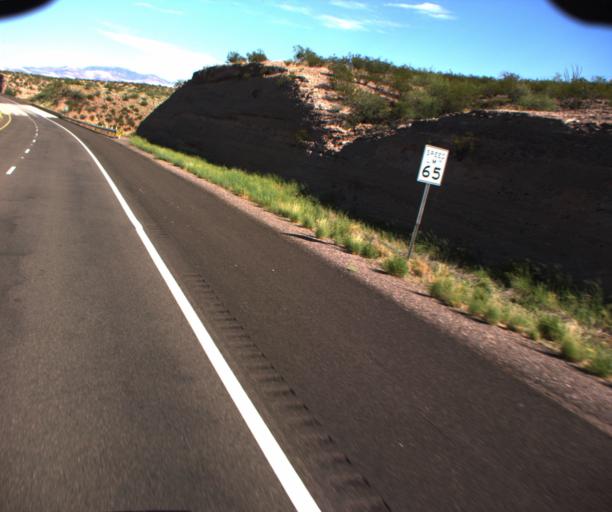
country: US
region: Arizona
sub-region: Greenlee County
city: Clifton
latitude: 32.9706
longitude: -109.2381
